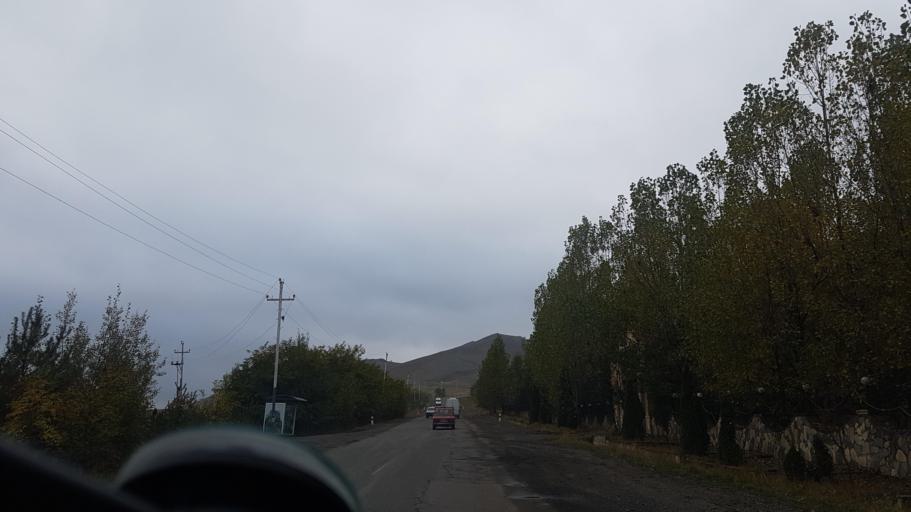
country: AZ
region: Gadabay Rayon
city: Ariqdam
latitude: 40.6301
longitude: 45.8144
